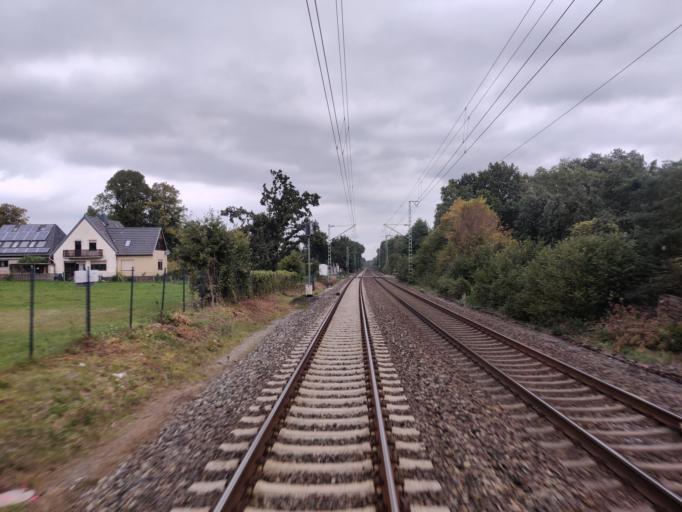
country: DE
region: Lower Saxony
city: Ritterhude
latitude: 53.1980
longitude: 8.7677
